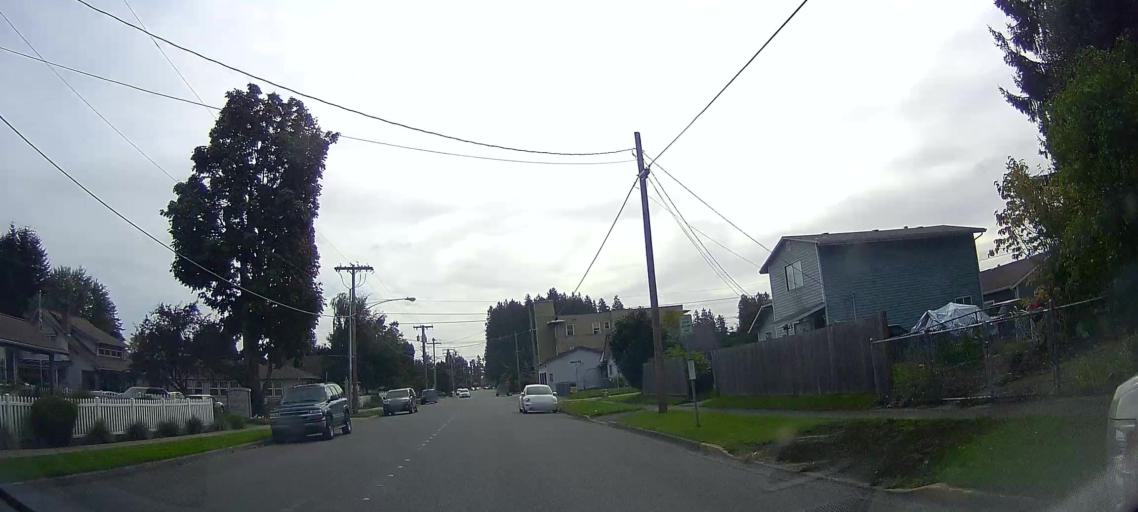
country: US
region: Washington
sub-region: Skagit County
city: Burlington
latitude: 48.4766
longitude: -122.3192
